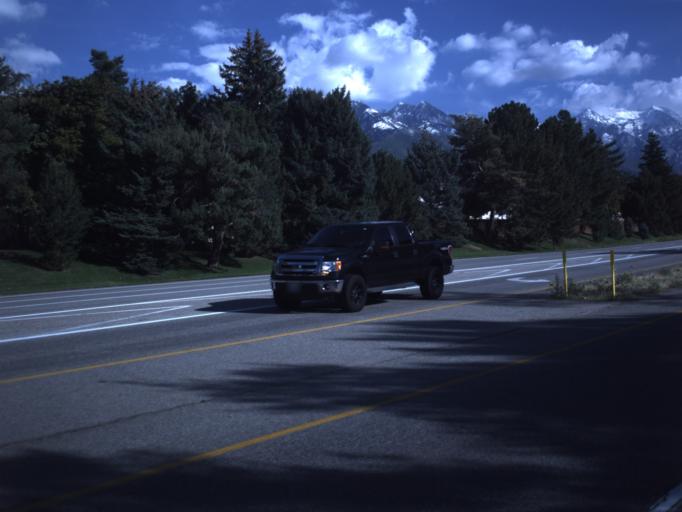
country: US
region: Utah
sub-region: Salt Lake County
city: Holladay
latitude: 40.6490
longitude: -111.8486
